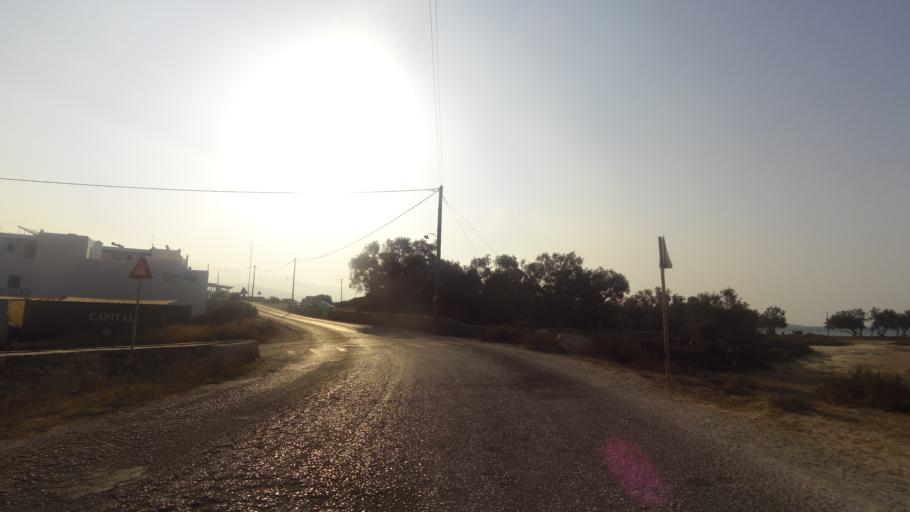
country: GR
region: South Aegean
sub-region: Nomos Kykladon
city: Antiparos
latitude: 37.0376
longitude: 25.0827
